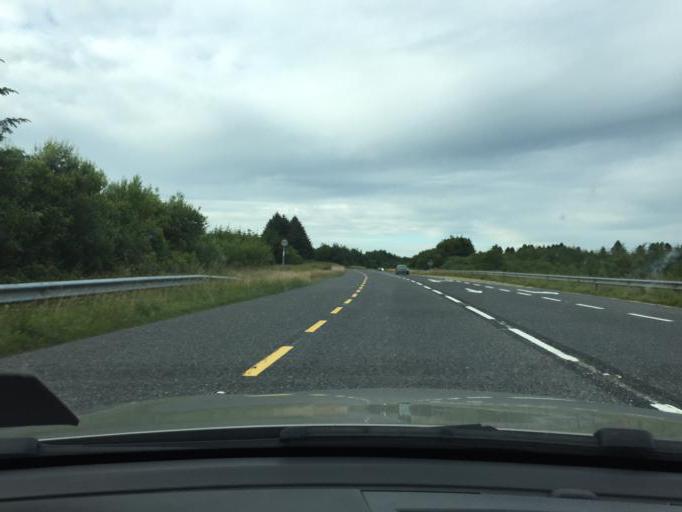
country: IE
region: Munster
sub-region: Waterford
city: Dungarvan
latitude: 52.0230
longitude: -7.6826
